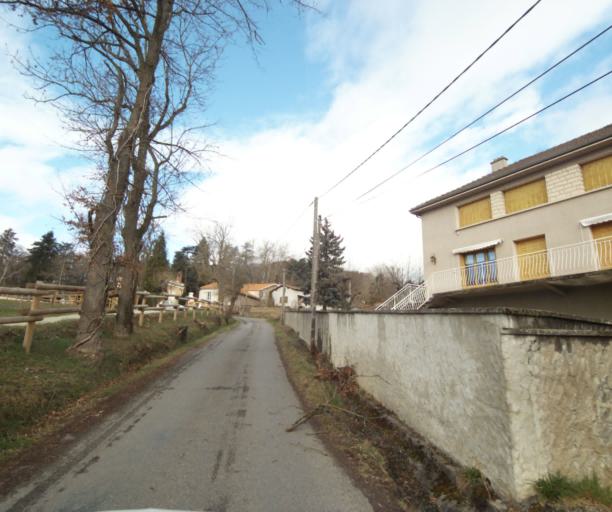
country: FR
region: Rhone-Alpes
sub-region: Departement de la Loire
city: La Talaudiere
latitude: 45.4807
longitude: 4.4121
